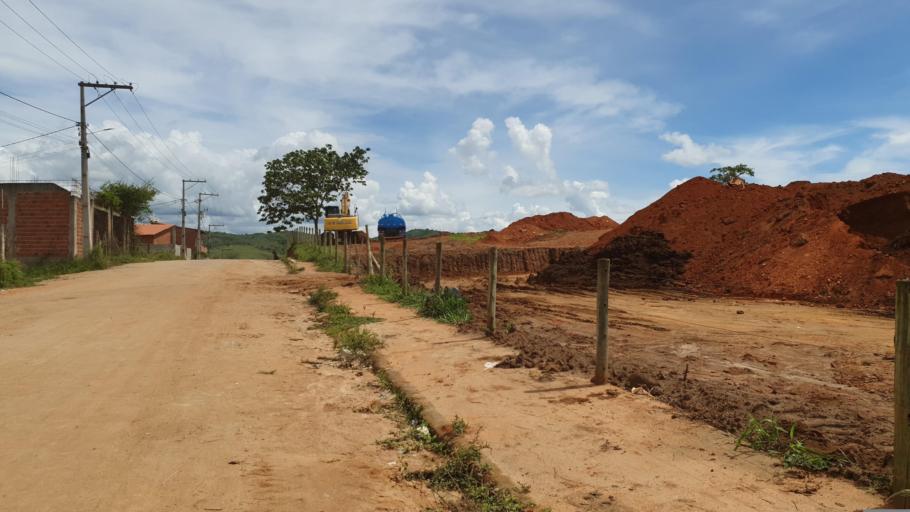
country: BR
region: Bahia
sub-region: Itagiba
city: Itagiba
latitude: -14.4265
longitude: -39.9057
